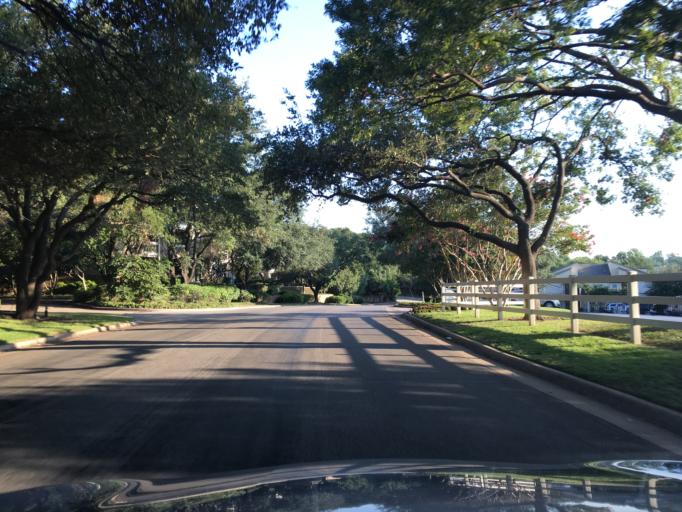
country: US
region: Texas
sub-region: Dallas County
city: Addison
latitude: 32.9671
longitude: -96.8142
